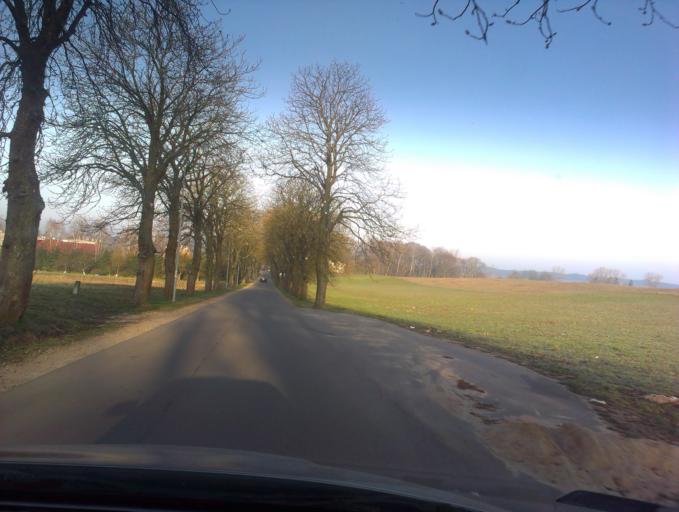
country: PL
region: West Pomeranian Voivodeship
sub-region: Powiat szczecinecki
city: Szczecinek
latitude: 53.7488
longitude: 16.6516
